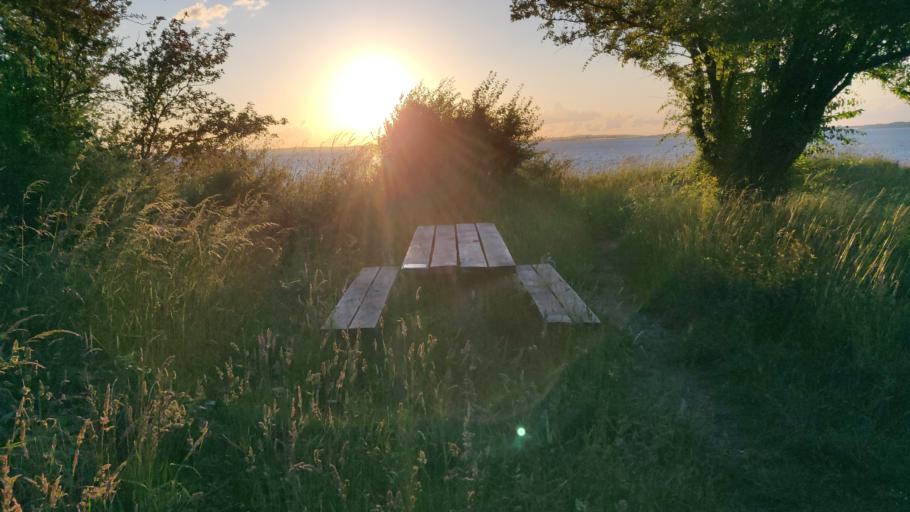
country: DK
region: Zealand
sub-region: Roskilde Kommune
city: Roskilde
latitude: 55.6874
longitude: 12.0767
